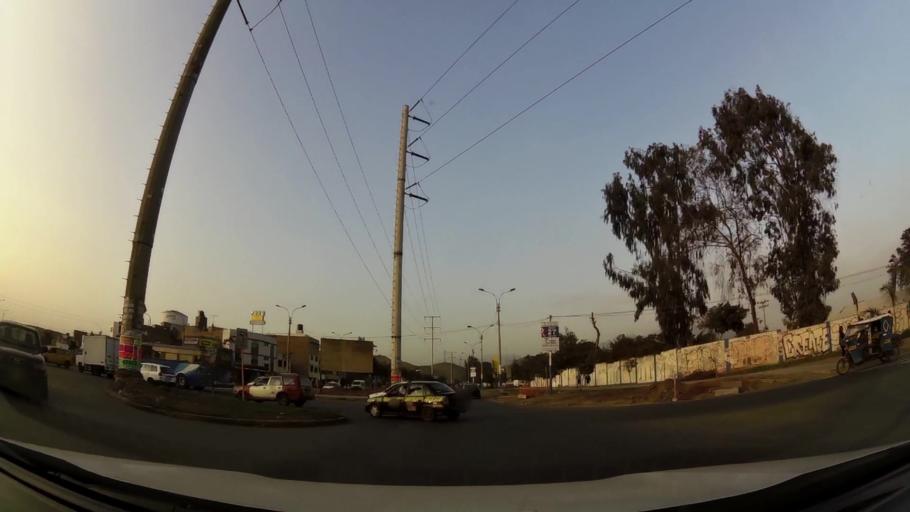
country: PE
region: Lima
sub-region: Lima
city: Independencia
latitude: -12.0097
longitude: -77.0877
